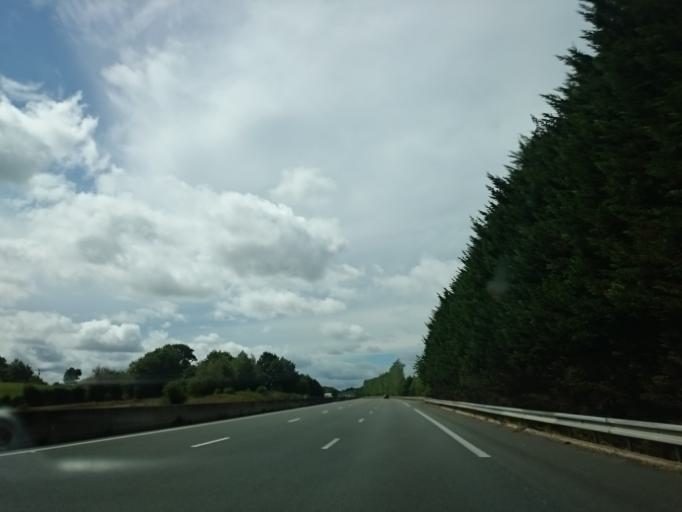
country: FR
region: Centre
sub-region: Departement d'Eure-et-Loir
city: La Bazoche-Gouet
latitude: 48.2246
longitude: 0.9732
